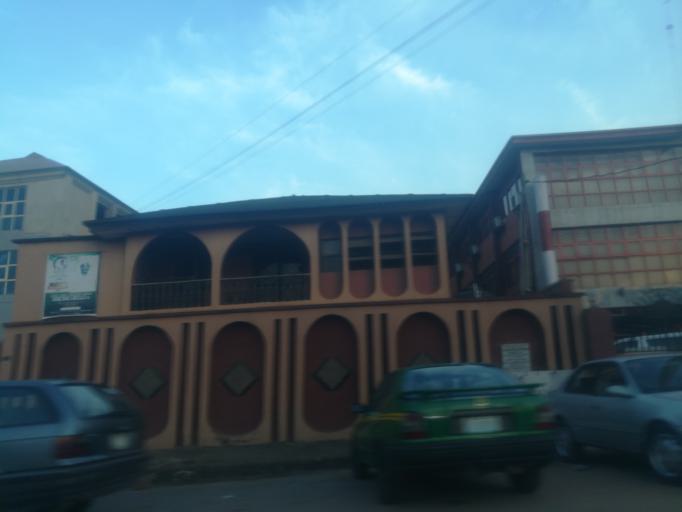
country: NG
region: Ogun
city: Abeokuta
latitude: 7.1439
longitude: 3.3381
